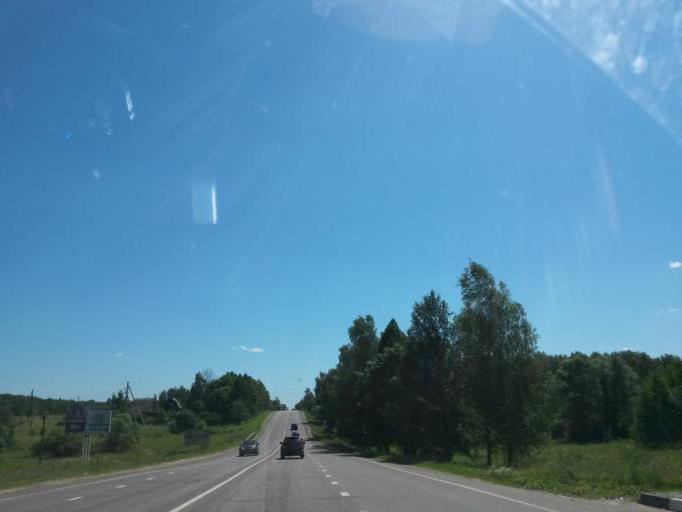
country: RU
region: Moskovskaya
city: Proletarskiy
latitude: 55.0406
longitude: 37.4303
